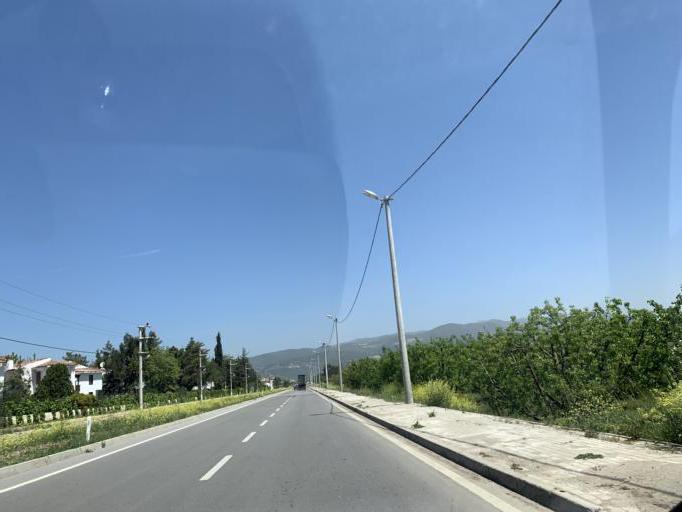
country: TR
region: Bursa
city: Iznik
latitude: 40.4069
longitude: 29.7039
